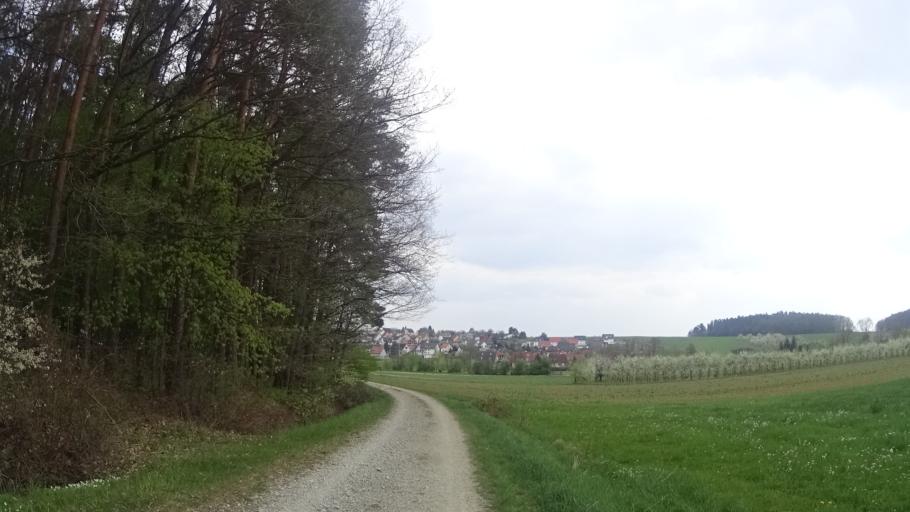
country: DE
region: Bavaria
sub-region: Upper Franconia
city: Igensdorf
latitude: 49.6198
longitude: 11.2181
